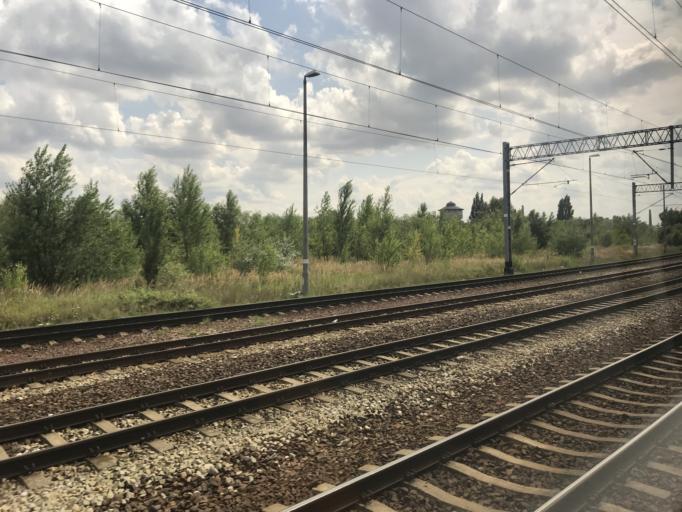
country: PL
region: Greater Poland Voivodeship
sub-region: Poznan
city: Poznan
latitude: 52.3905
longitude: 16.9068
